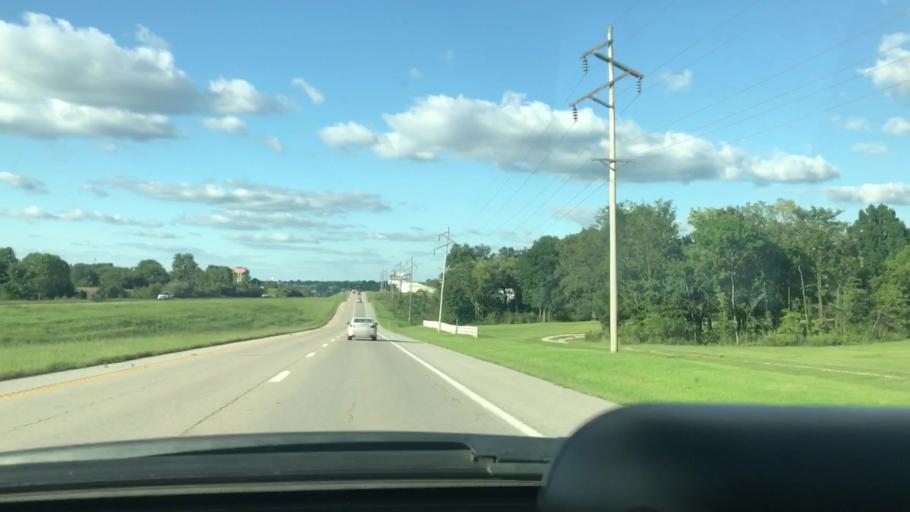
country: US
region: Missouri
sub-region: Pettis County
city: Sedalia
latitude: 38.6459
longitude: -93.2614
